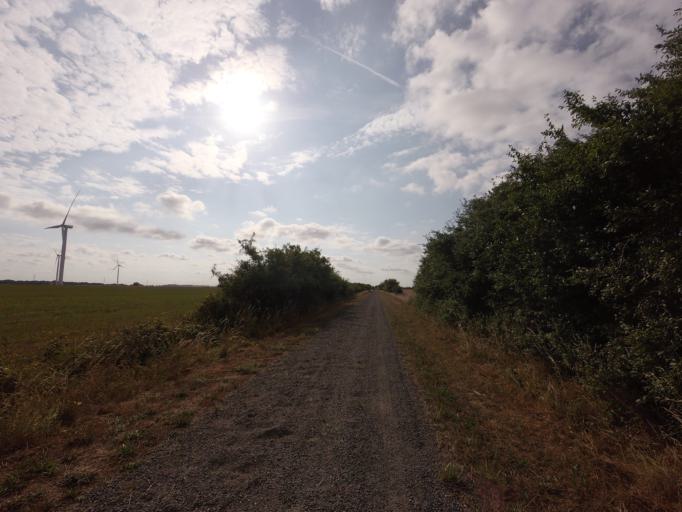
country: SE
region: Skane
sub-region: Helsingborg
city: Odakra
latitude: 56.1612
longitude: 12.7430
